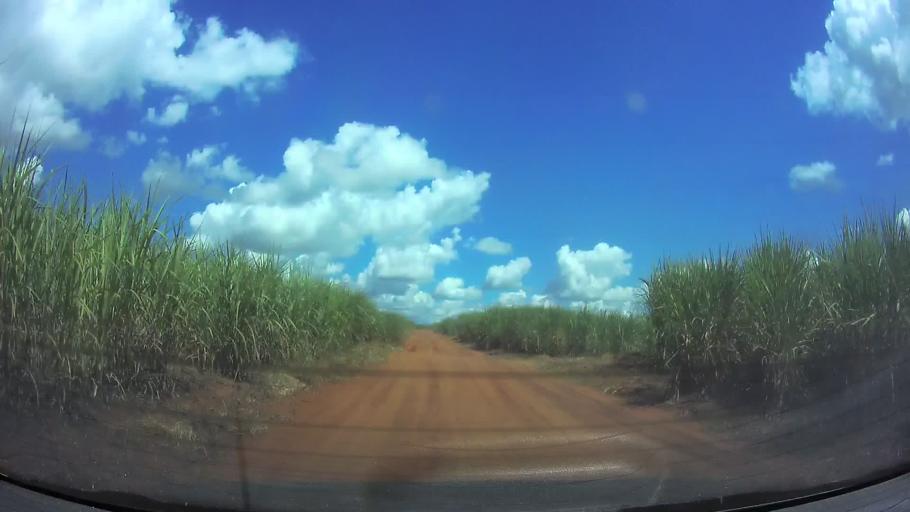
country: PY
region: Paraguari
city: La Colmena
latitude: -25.9608
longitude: -56.7638
